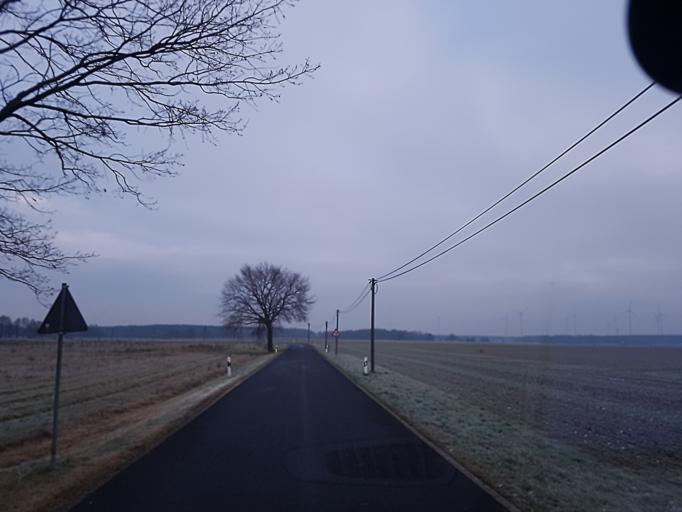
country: DE
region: Brandenburg
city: Crinitz
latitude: 51.7265
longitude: 13.8369
